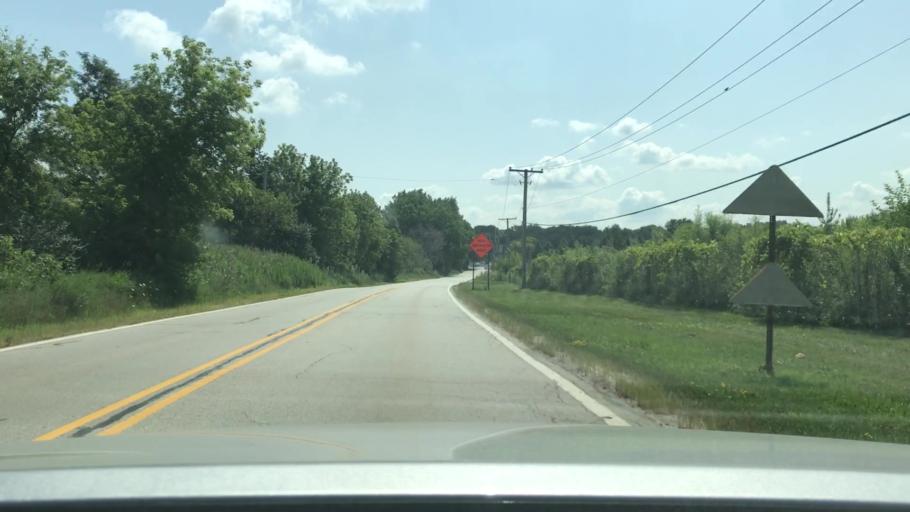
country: US
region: Illinois
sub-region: Will County
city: Bolingbrook
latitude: 41.7193
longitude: -88.0747
